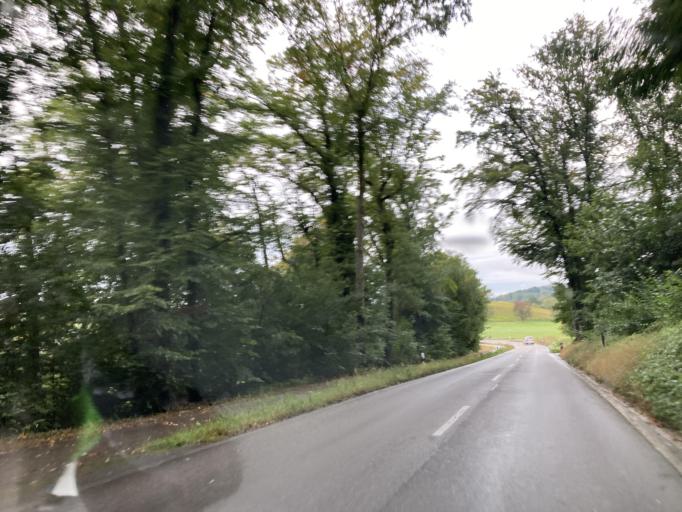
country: DE
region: Baden-Wuerttemberg
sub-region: Freiburg Region
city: Feldberg
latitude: 47.7811
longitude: 7.6223
